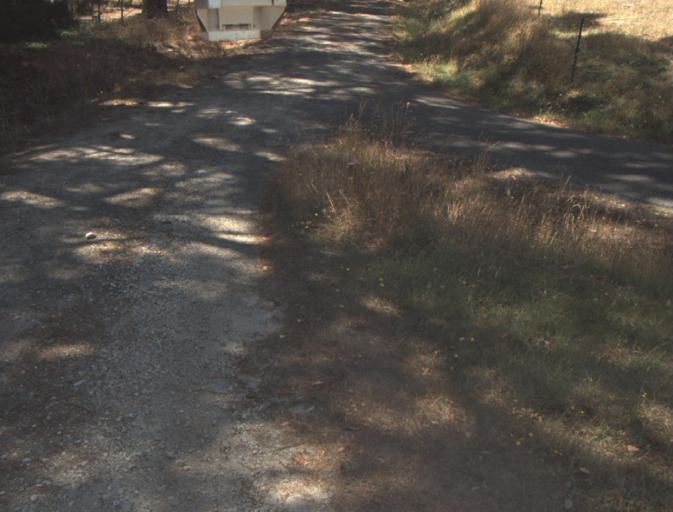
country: AU
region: Tasmania
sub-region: Launceston
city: Mayfield
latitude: -41.2588
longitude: 147.1436
